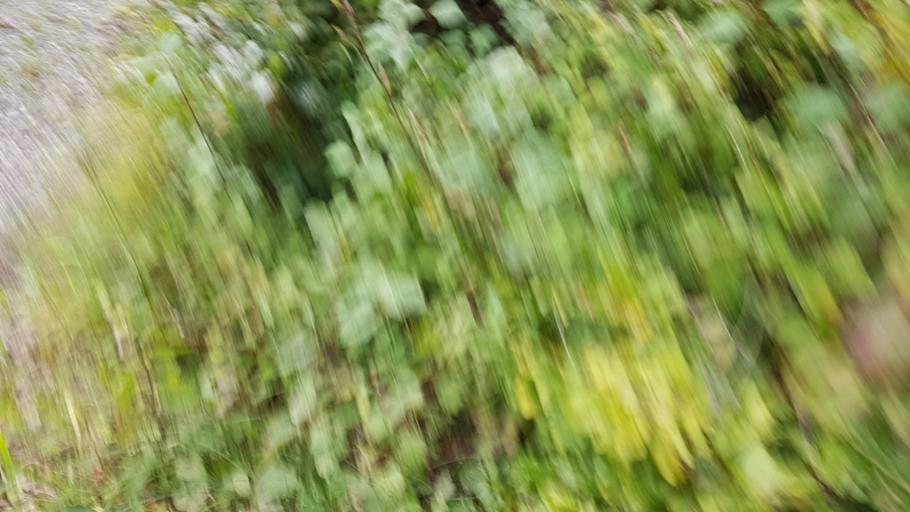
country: CH
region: Bern
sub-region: Bern-Mittelland District
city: Konolfingen
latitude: 46.8610
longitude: 7.6334
